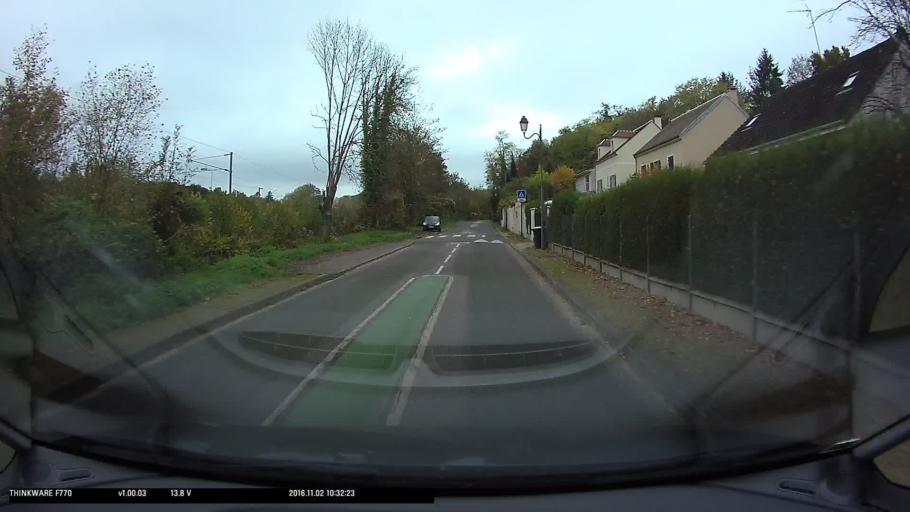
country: FR
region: Ile-de-France
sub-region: Departement du Val-d'Oise
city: Ableiges
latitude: 49.0812
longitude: 2.0027
